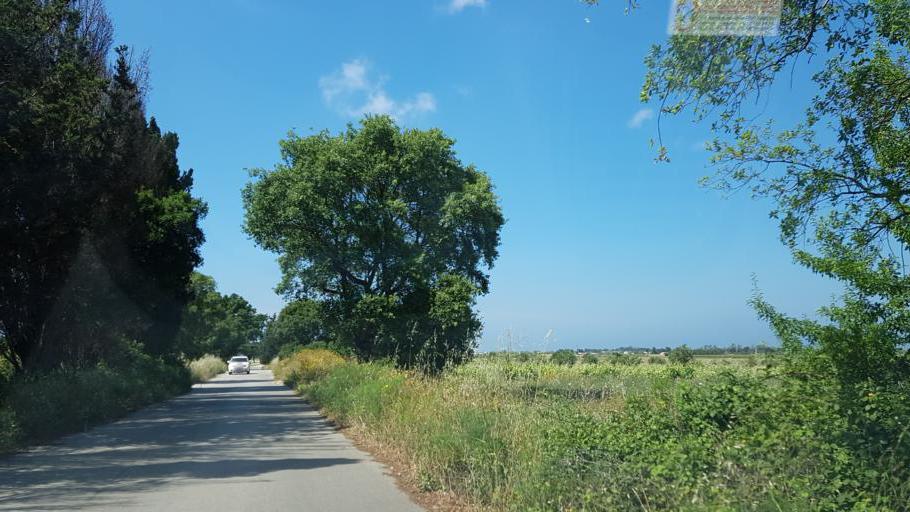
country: IT
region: Apulia
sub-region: Provincia di Brindisi
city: Brindisi
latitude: 40.6509
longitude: 17.8546
